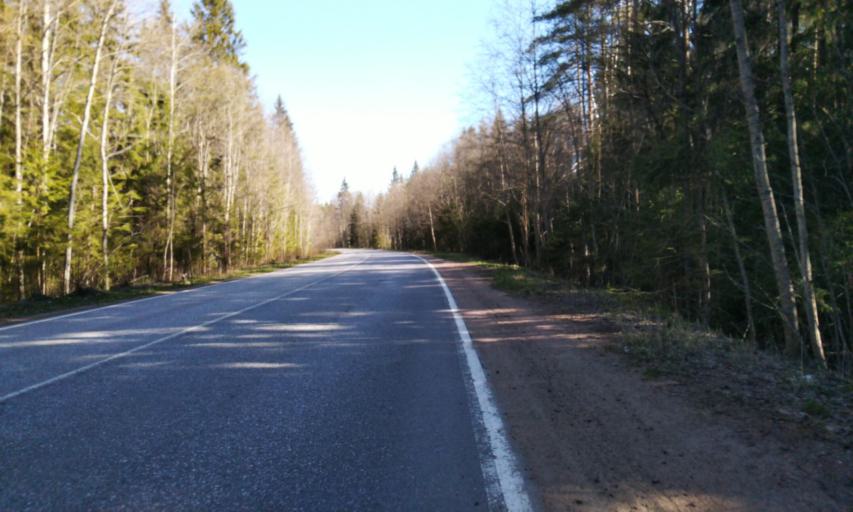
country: RU
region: Leningrad
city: Garbolovo
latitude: 60.3482
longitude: 30.4424
